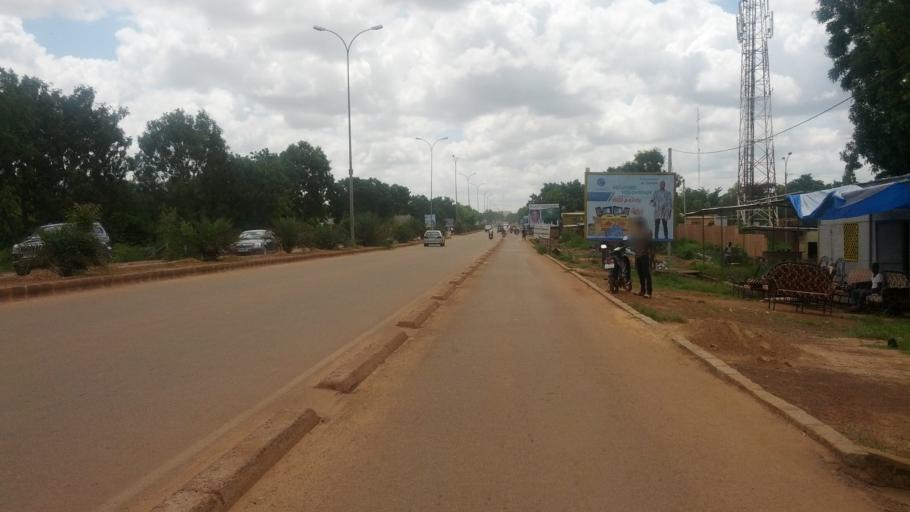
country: BF
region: Centre
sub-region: Kadiogo Province
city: Ouagadougou
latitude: 12.3757
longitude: -1.5003
